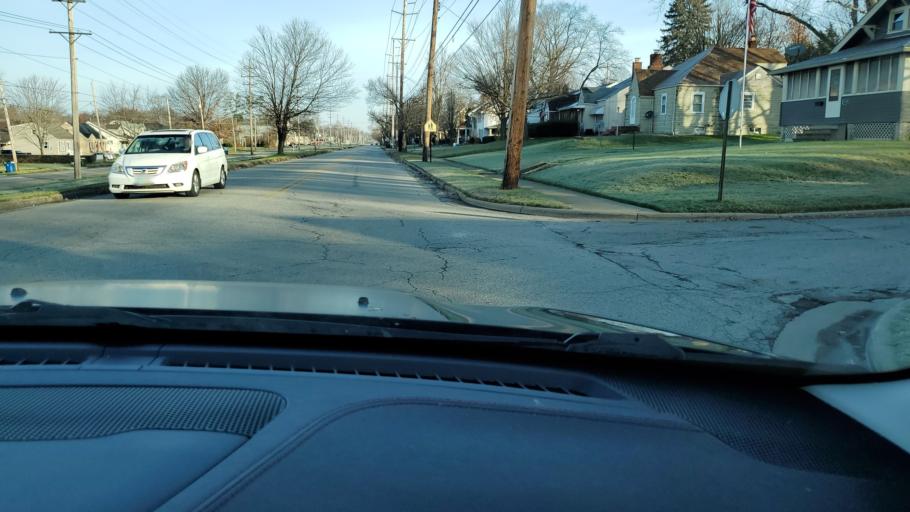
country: US
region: Ohio
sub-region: Mahoning County
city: Boardman
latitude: 41.0416
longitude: -80.6575
